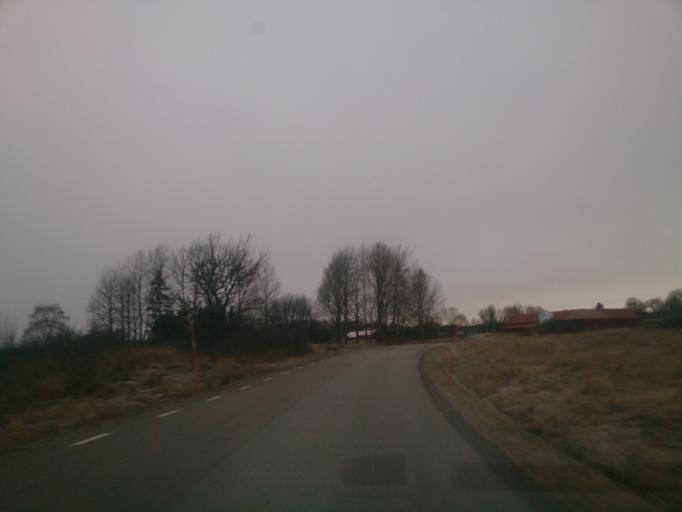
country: SE
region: OEstergoetland
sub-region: Norrkopings Kommun
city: Krokek
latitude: 58.5134
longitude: 16.5246
